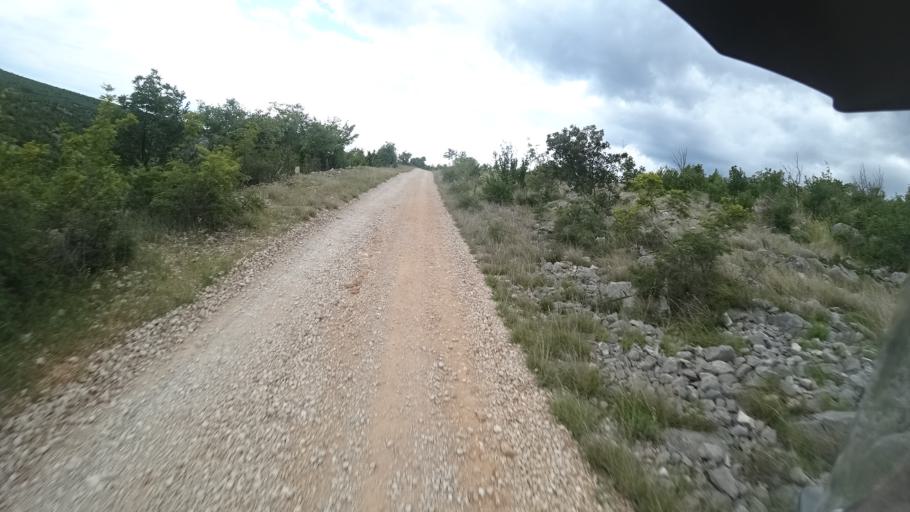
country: HR
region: Sibensko-Kniniska
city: Kistanje
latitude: 44.0970
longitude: 16.0152
